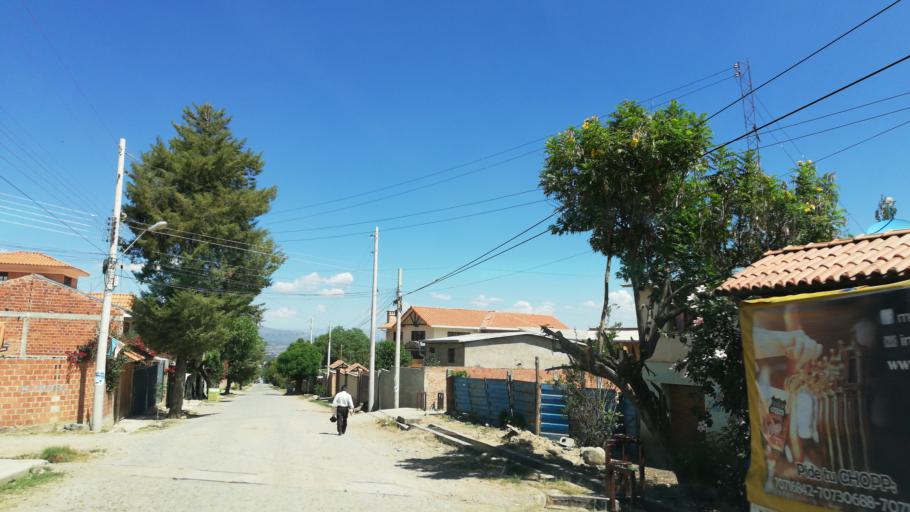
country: BO
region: Cochabamba
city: Cochabamba
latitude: -17.3295
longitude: -66.2151
